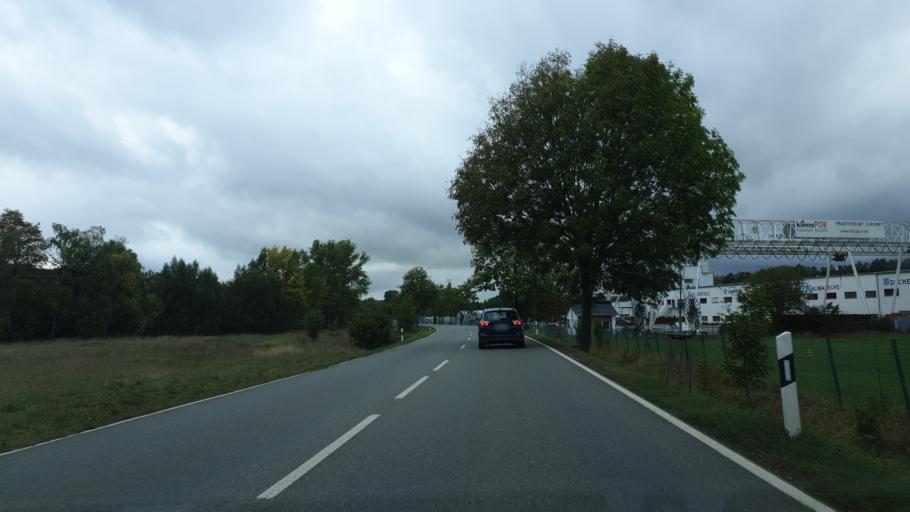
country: DE
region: Saxony
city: Glauchau
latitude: 50.8252
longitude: 12.5613
